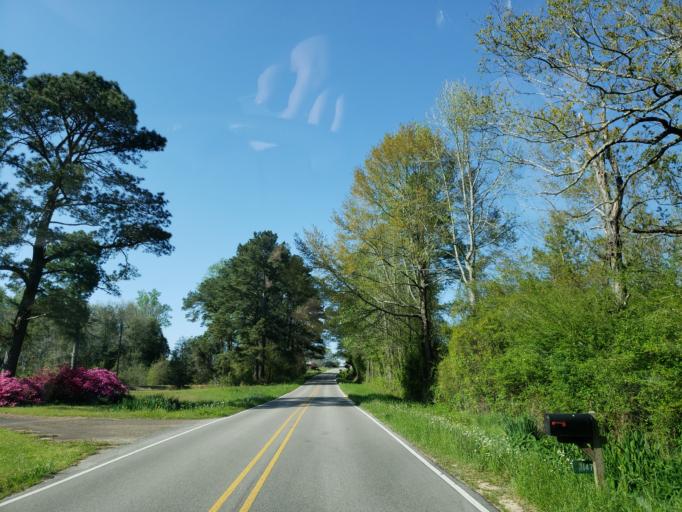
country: US
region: Mississippi
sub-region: Forrest County
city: Rawls Springs
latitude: 31.5526
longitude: -89.3658
